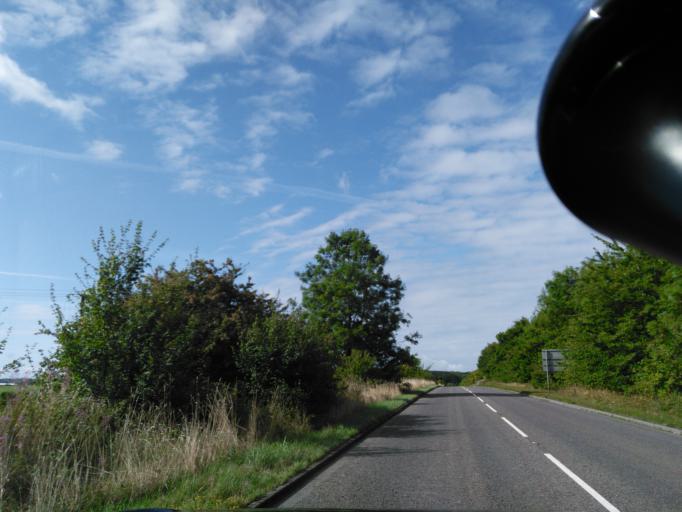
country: GB
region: England
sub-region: Wiltshire
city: Upton Scudamore
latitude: 51.2223
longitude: -2.1941
